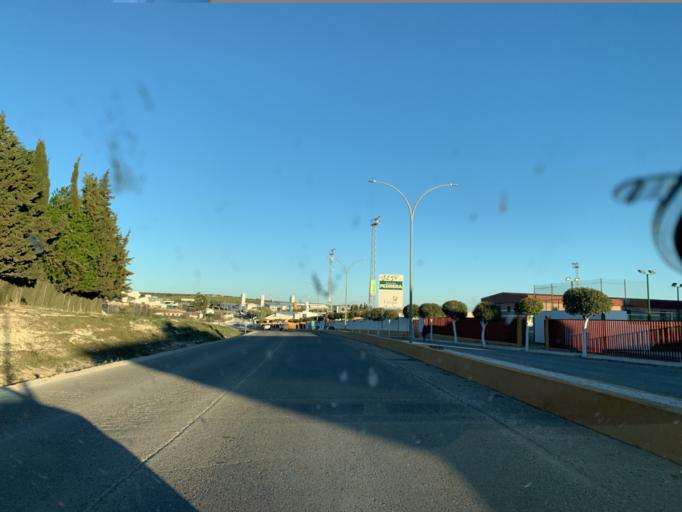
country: ES
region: Andalusia
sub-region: Provincia de Sevilla
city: Pedrera
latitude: 37.2309
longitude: -4.8968
